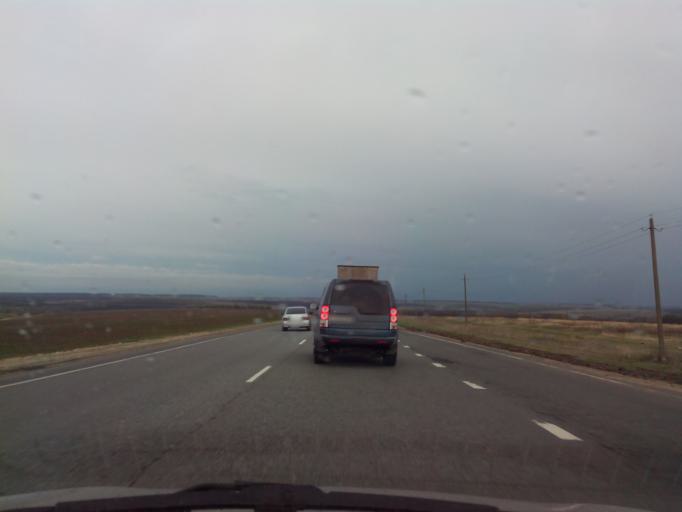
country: RU
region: Moskovskaya
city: Uzunovo
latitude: 54.4909
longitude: 38.5137
